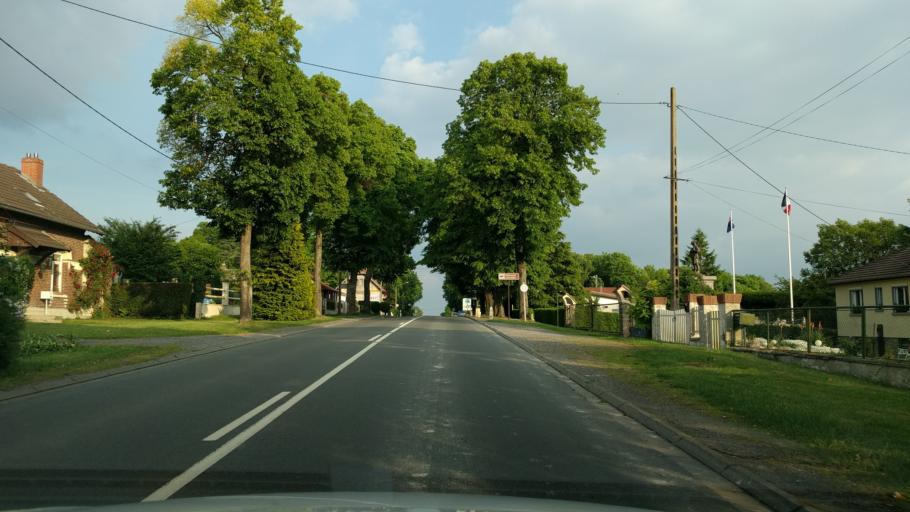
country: FR
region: Picardie
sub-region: Departement de la Somme
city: Peronne
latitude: 49.9479
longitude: 2.9321
